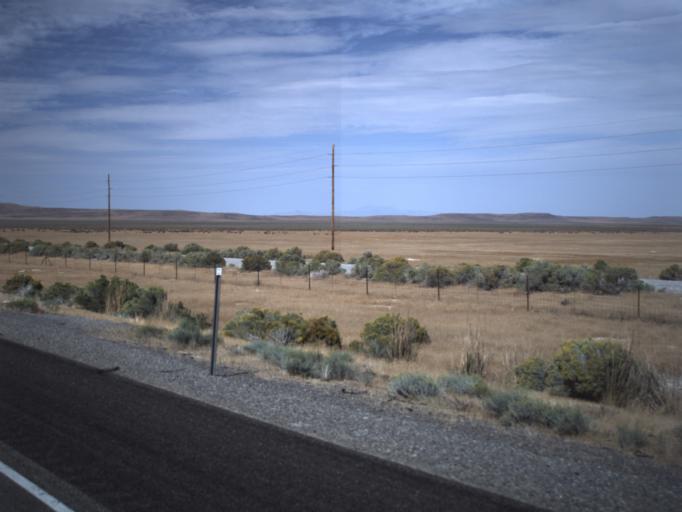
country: US
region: Utah
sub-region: Tooele County
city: Grantsville
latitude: 40.7531
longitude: -113.0387
